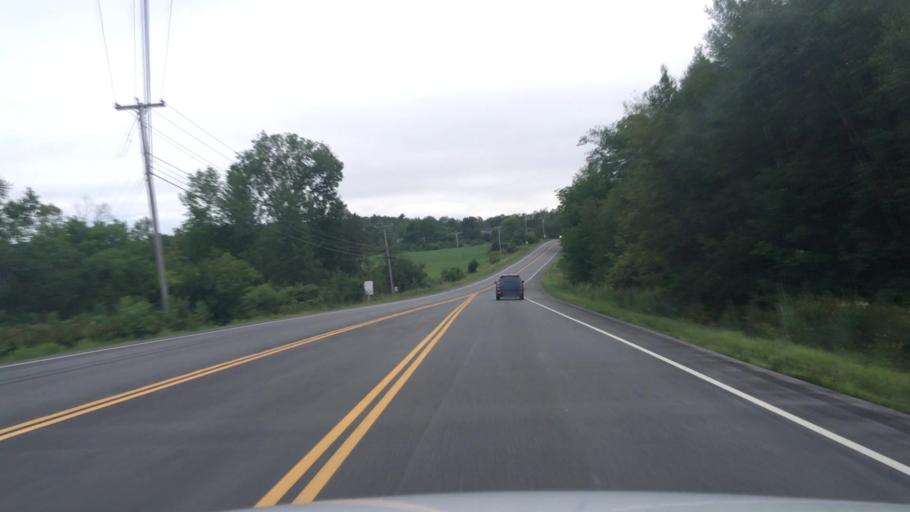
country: US
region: Maine
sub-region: Waldo County
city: Belfast
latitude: 44.4194
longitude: -69.0370
